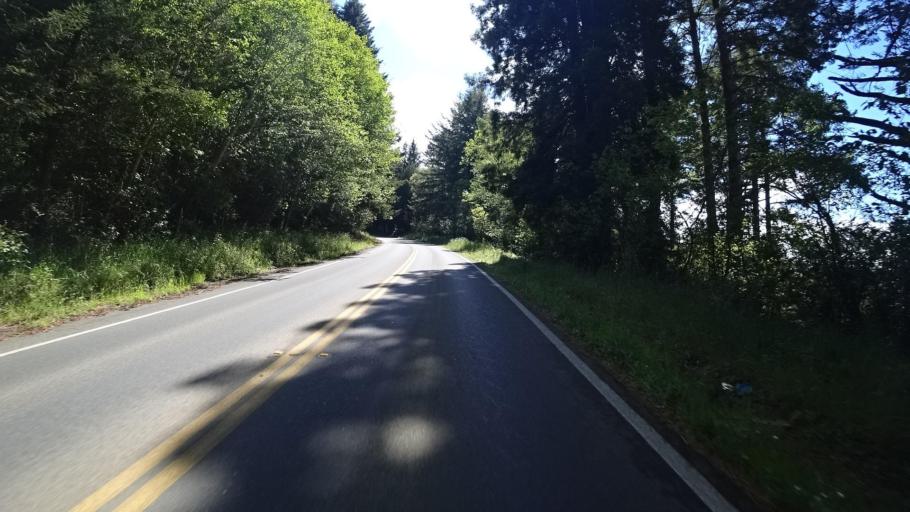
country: US
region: California
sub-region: Humboldt County
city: McKinleyville
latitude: 40.9542
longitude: -124.0832
